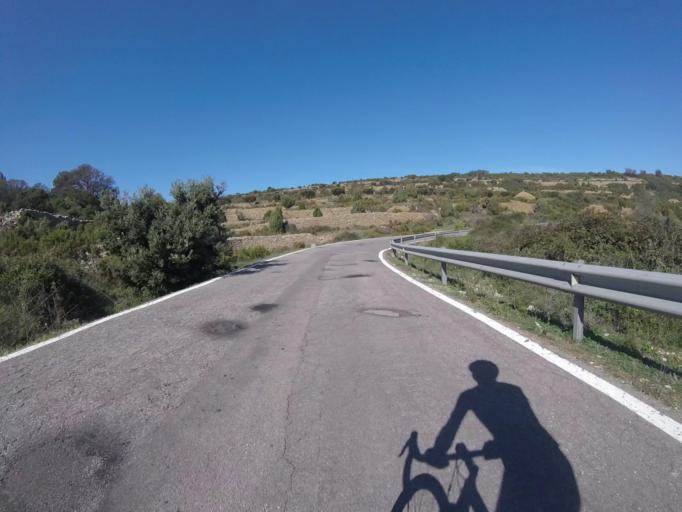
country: ES
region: Valencia
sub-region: Provincia de Castello
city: Sarratella
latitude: 40.3249
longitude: 0.0266
